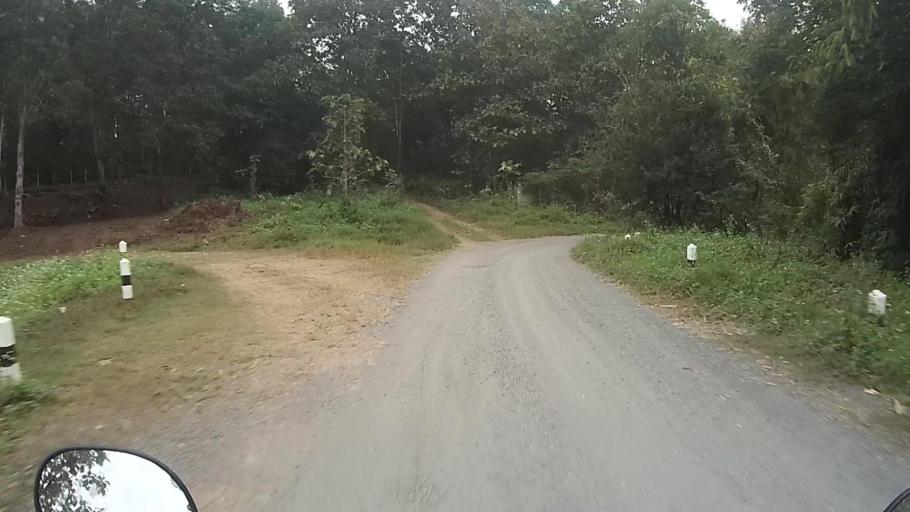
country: TH
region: Chiang Mai
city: Mae On
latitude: 18.8600
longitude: 99.2424
